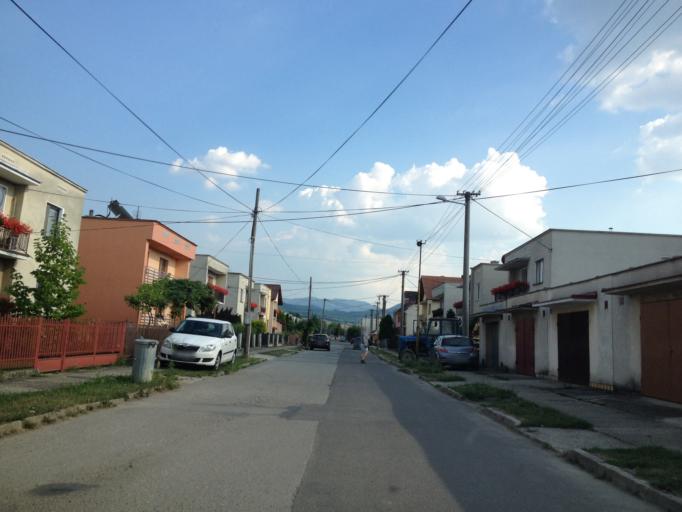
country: SK
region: Nitriansky
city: Puchov
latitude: 49.0712
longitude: 18.3309
